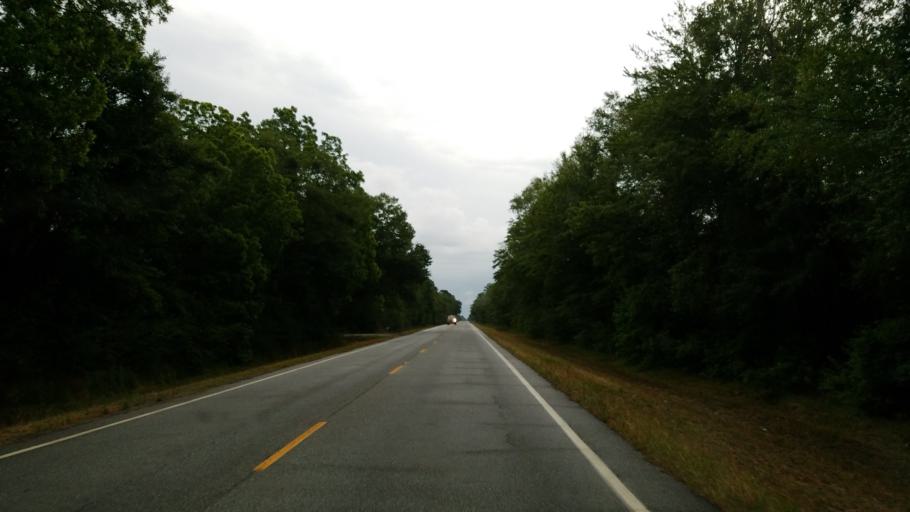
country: US
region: Georgia
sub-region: Berrien County
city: Ray City
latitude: 31.0969
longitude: -83.2639
